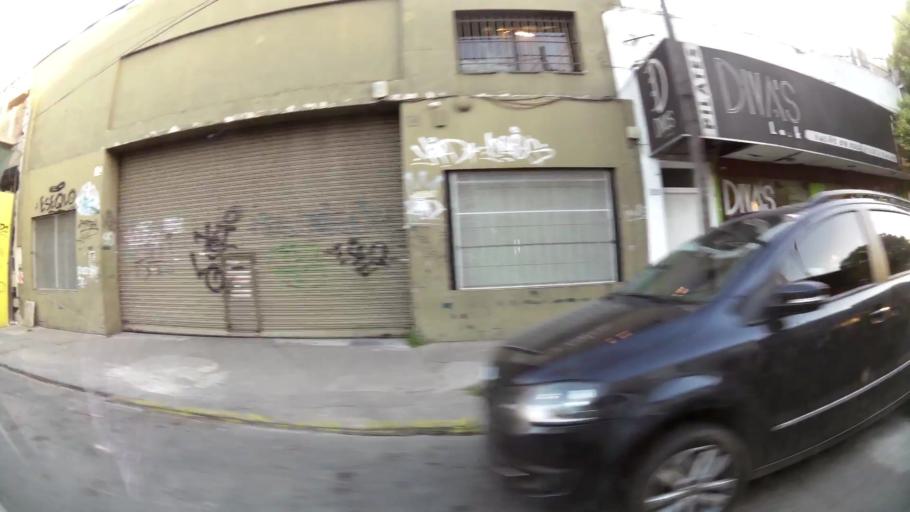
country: AR
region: Buenos Aires
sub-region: Partido de Vicente Lopez
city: Olivos
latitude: -34.5349
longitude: -58.5061
